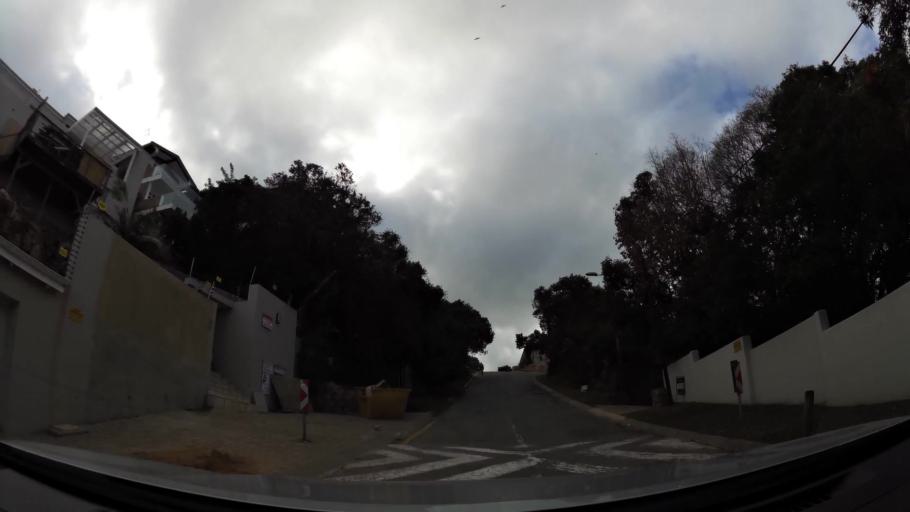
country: ZA
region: Western Cape
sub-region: Eden District Municipality
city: Plettenberg Bay
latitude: -34.0588
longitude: 23.3769
